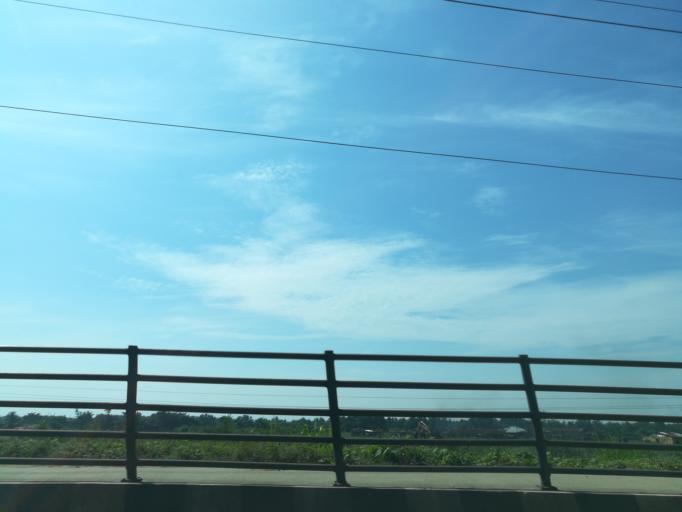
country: NG
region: Lagos
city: Ebute Ikorodu
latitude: 6.6094
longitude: 3.4397
